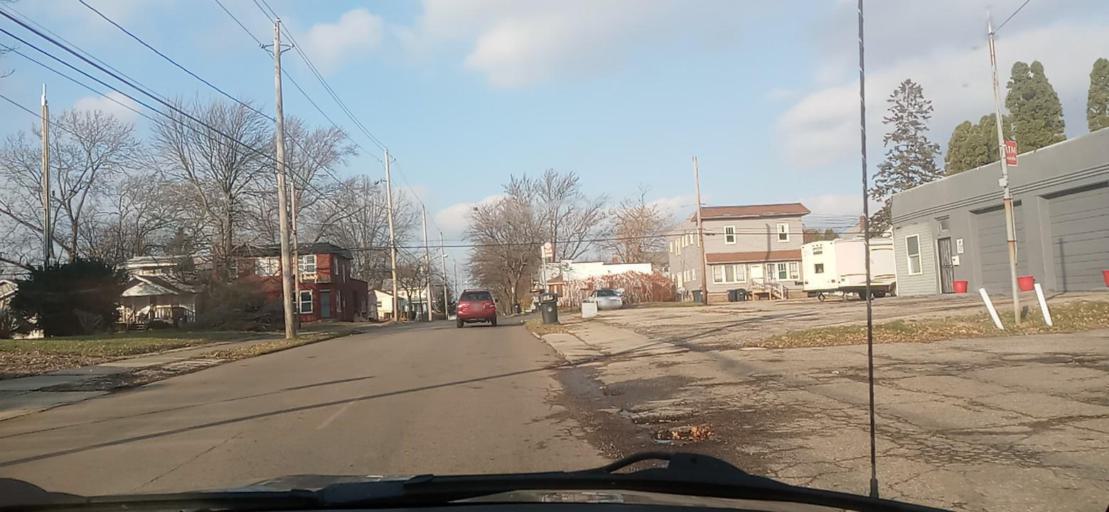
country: US
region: Ohio
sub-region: Summit County
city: Akron
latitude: 41.0540
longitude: -81.5573
